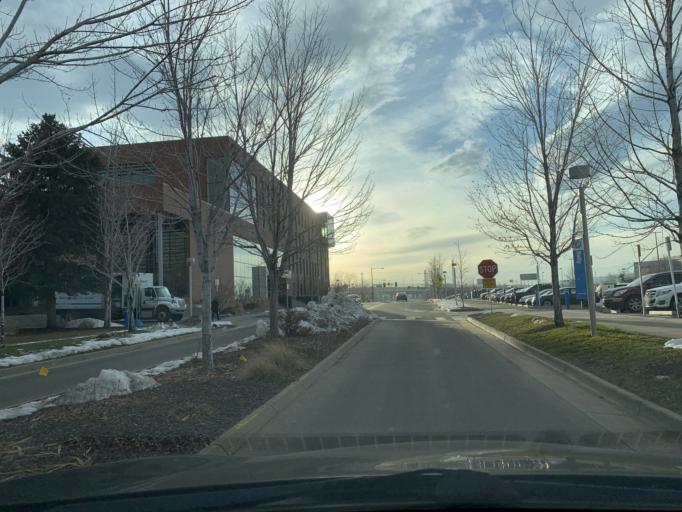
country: US
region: Colorado
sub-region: Denver County
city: Denver
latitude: 39.7420
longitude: -105.0045
